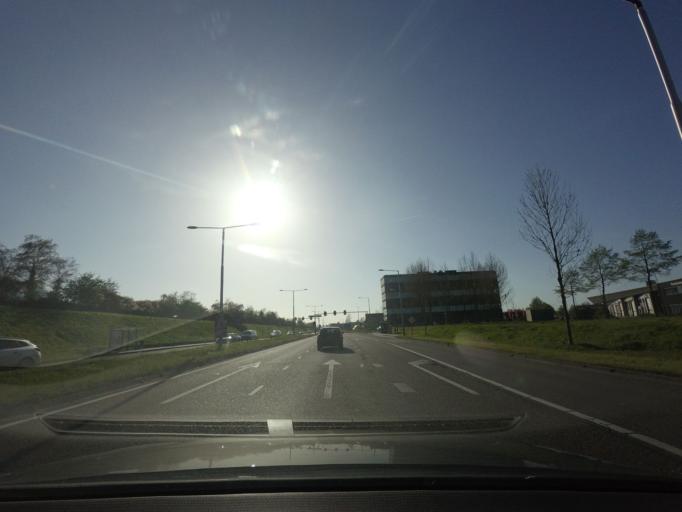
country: NL
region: Utrecht
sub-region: Gemeente Amersfoort
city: Hoogland
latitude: 52.1949
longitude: 5.3912
